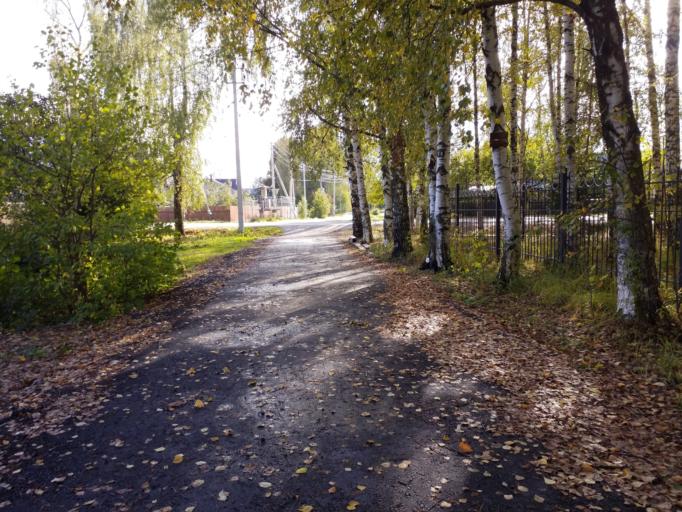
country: RU
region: Moskovskaya
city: Ashukino
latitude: 56.1600
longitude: 37.9529
